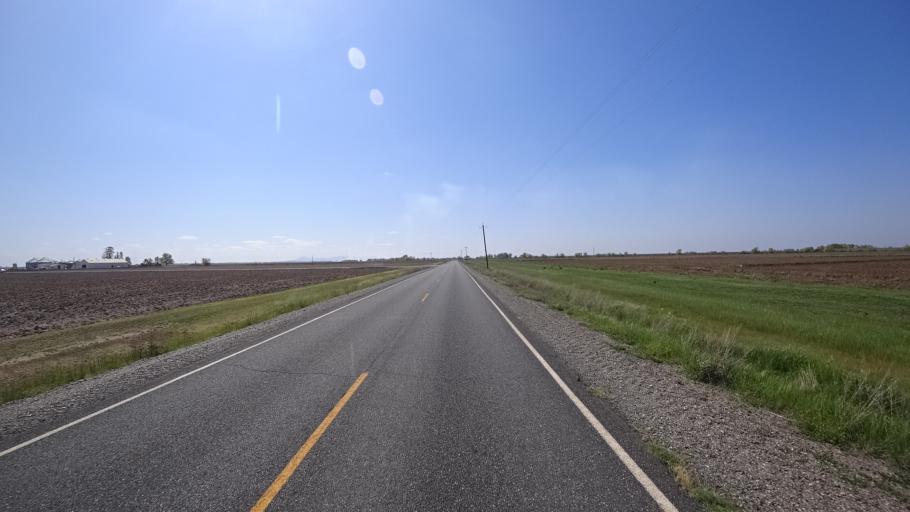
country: US
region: California
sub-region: Butte County
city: Durham
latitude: 39.4968
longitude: -121.9299
